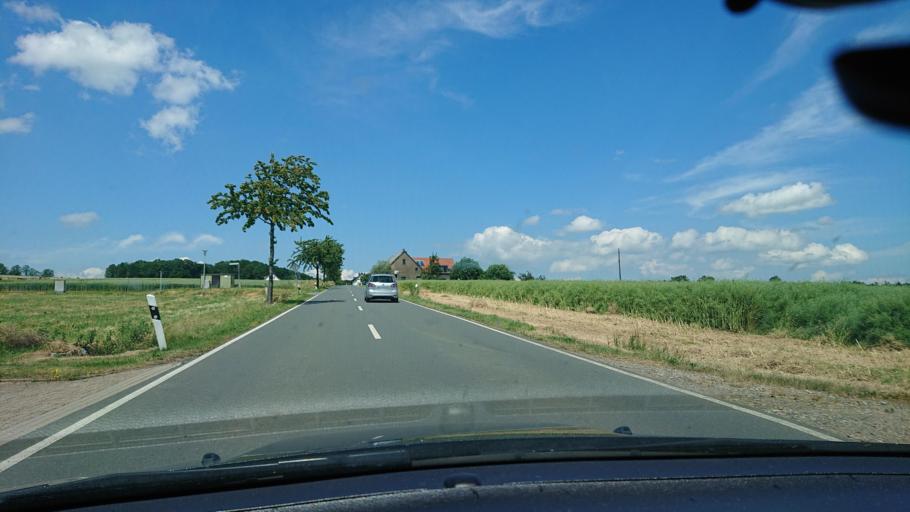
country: DE
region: North Rhine-Westphalia
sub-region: Regierungsbezirk Detmold
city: Rodinghausen
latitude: 52.2795
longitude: 8.4619
